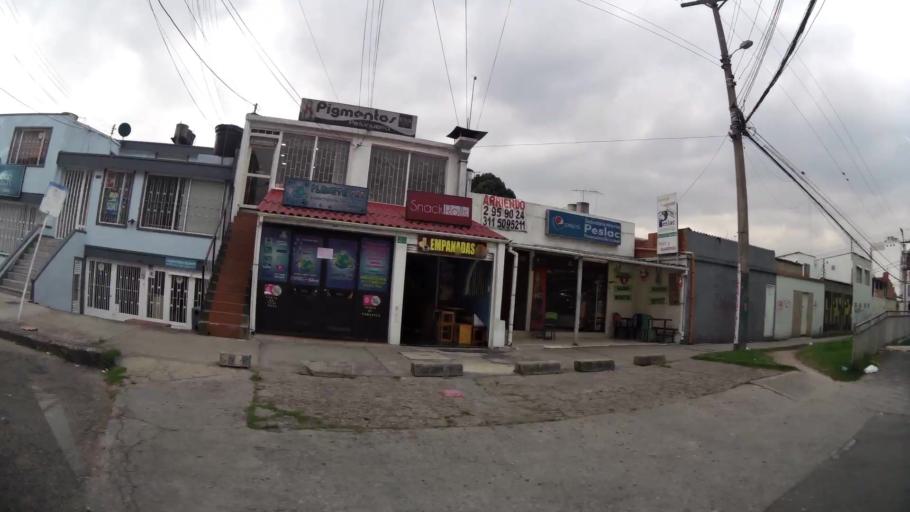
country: CO
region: Bogota D.C.
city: Bogota
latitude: 4.6699
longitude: -74.1069
